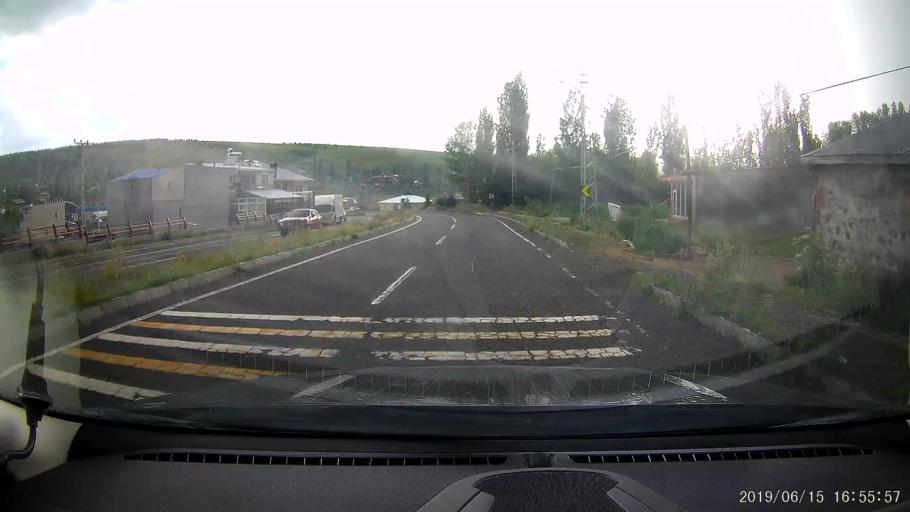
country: TR
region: Kars
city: Susuz
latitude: 40.7824
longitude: 43.1280
